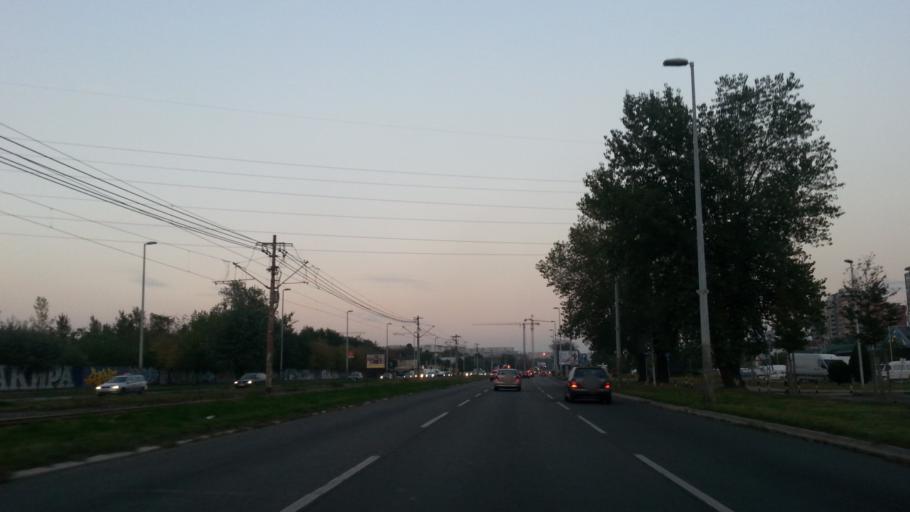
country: RS
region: Central Serbia
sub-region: Belgrade
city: Novi Beograd
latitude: 44.8038
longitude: 20.3913
